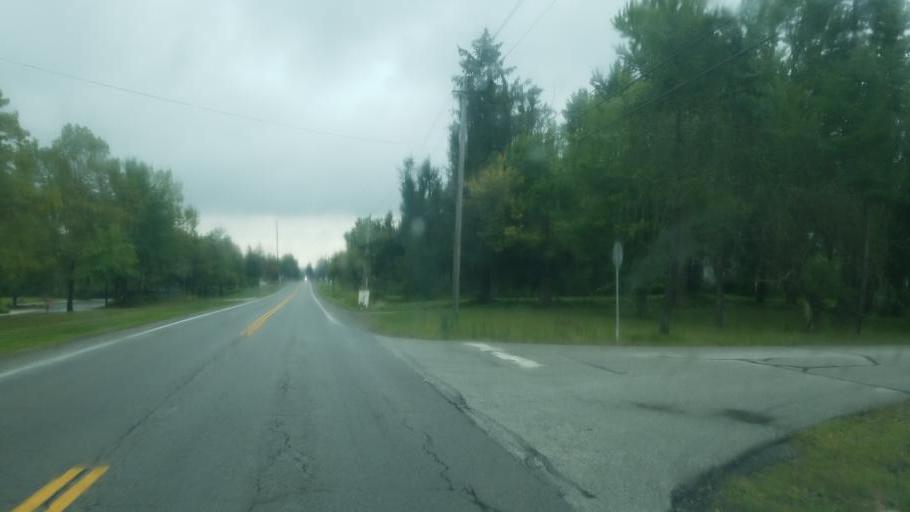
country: US
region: Ohio
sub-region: Geauga County
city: Burton
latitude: 41.5088
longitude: -81.1936
